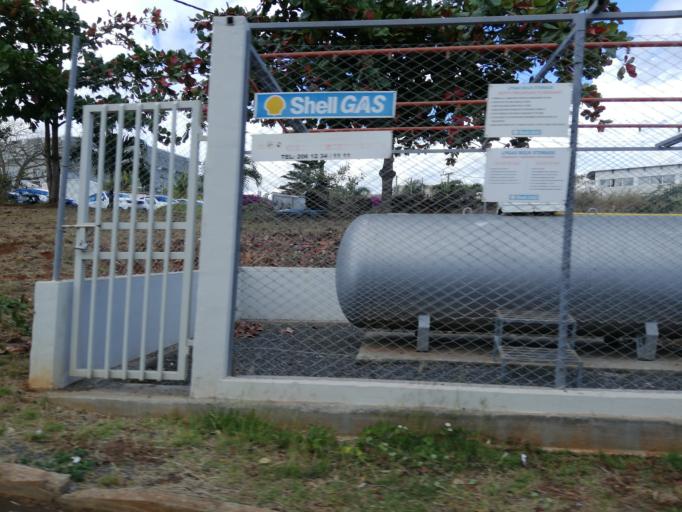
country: MU
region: Black River
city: Petite Riviere
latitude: -20.1895
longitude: 57.4652
